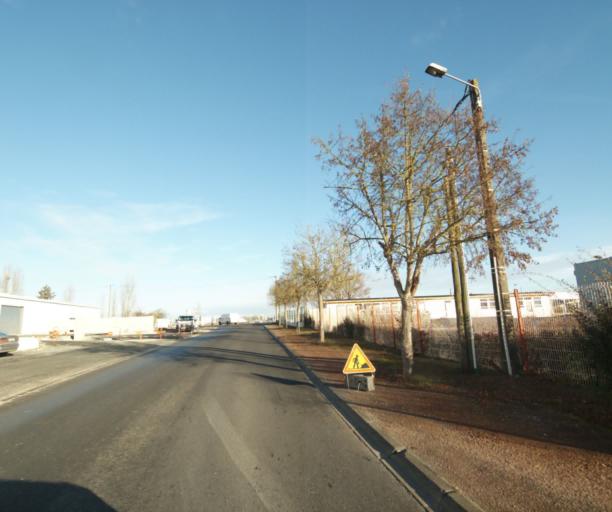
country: FR
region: Poitou-Charentes
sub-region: Departement de la Charente-Maritime
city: Saintes
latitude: 45.7425
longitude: -0.6626
